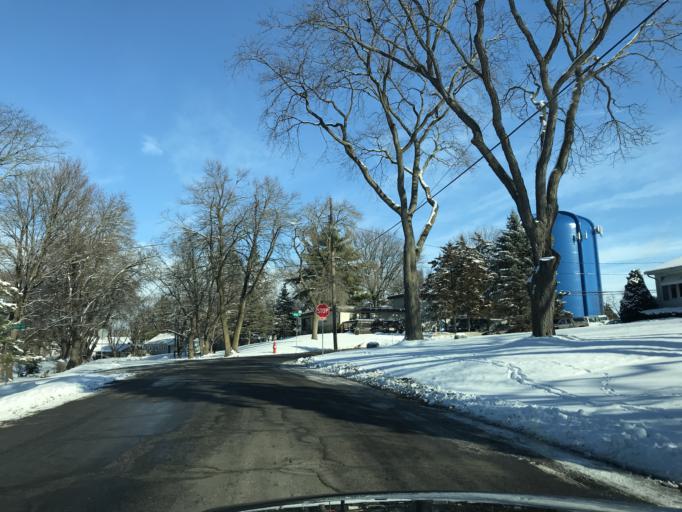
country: US
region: Wisconsin
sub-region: Dane County
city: Monona
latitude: 43.0709
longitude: -89.3172
